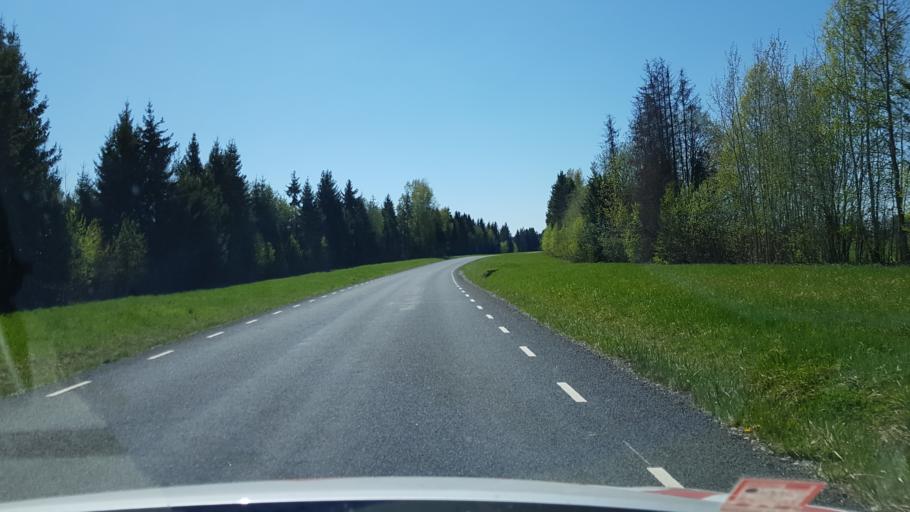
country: EE
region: Vorumaa
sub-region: Voru linn
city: Voru
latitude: 57.9560
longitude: 26.9627
